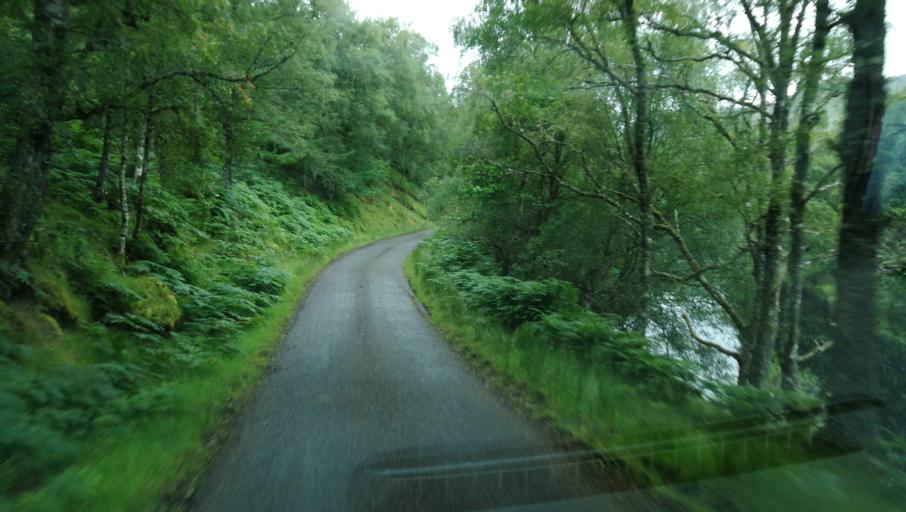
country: GB
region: Scotland
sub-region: Highland
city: Beauly
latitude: 57.3624
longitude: -4.8276
